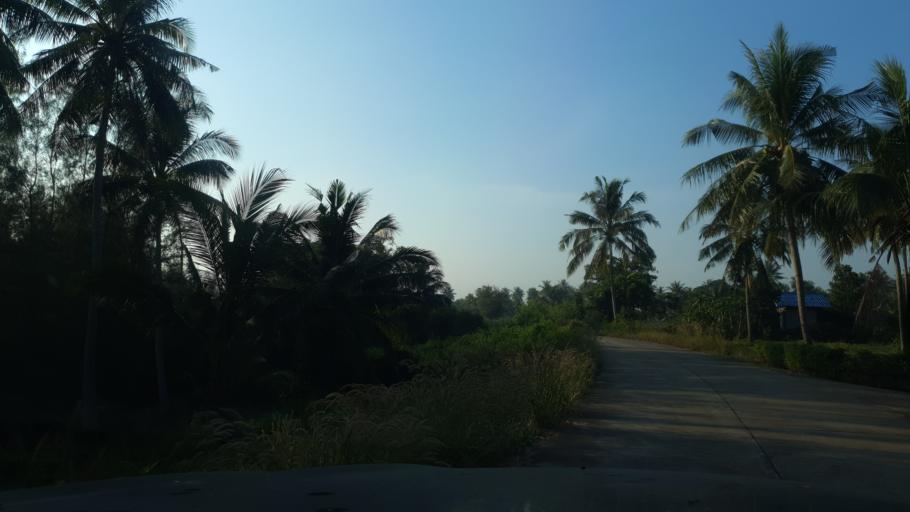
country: TH
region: Prachuap Khiri Khan
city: Bang Saphan
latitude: 11.2976
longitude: 99.5494
